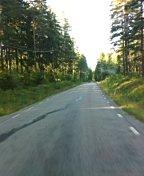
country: SE
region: Uppsala
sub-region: Habo Kommun
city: Balsta
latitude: 59.7019
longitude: 17.5373
